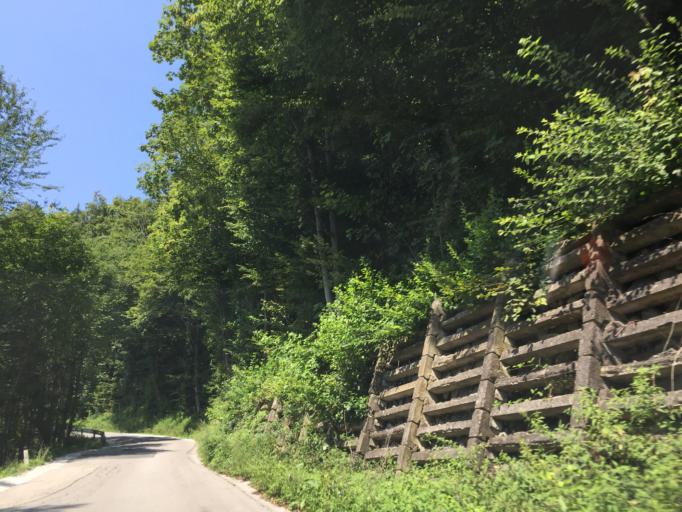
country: SI
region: Trbovlje
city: Trbovlje
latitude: 46.1789
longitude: 15.0499
